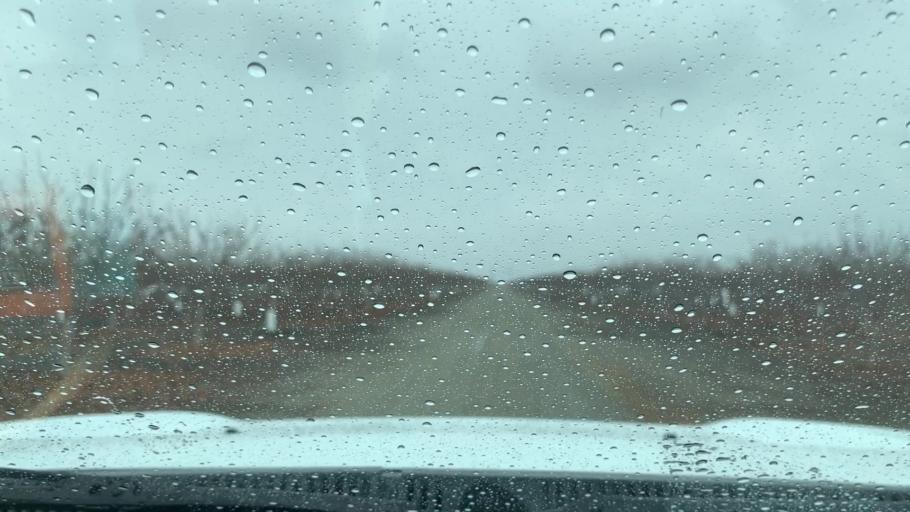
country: US
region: California
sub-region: Kings County
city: Corcoran
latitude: 36.0290
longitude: -119.4977
